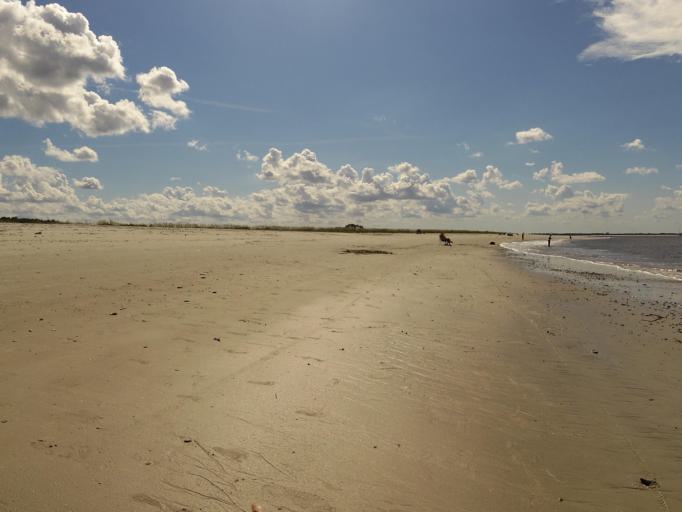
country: US
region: Florida
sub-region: Nassau County
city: Fernandina Beach
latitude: 30.7009
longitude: -81.4282
